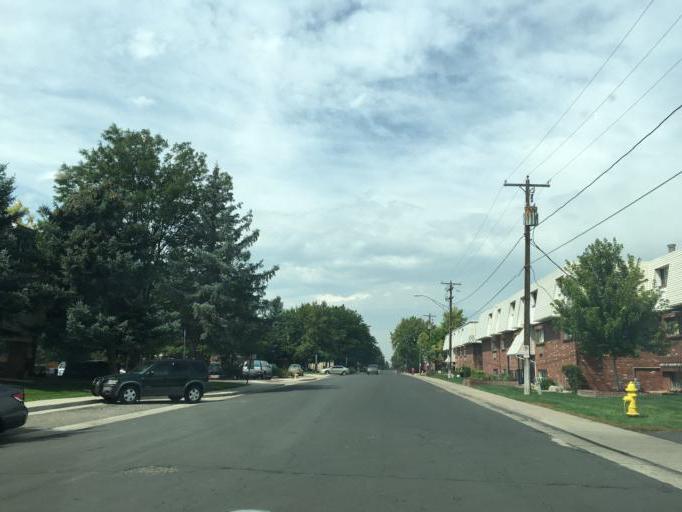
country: US
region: Colorado
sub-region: Adams County
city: Aurora
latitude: 39.7375
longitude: -104.8022
